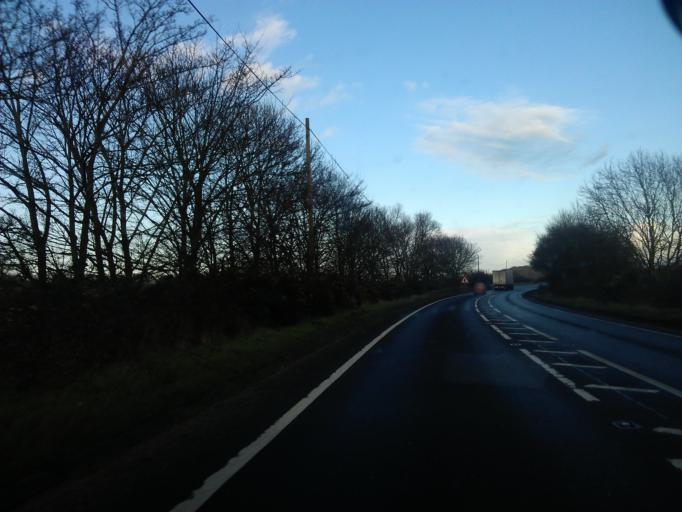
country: GB
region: England
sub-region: Suffolk
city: Shotley Gate
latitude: 51.9339
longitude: 1.2265
